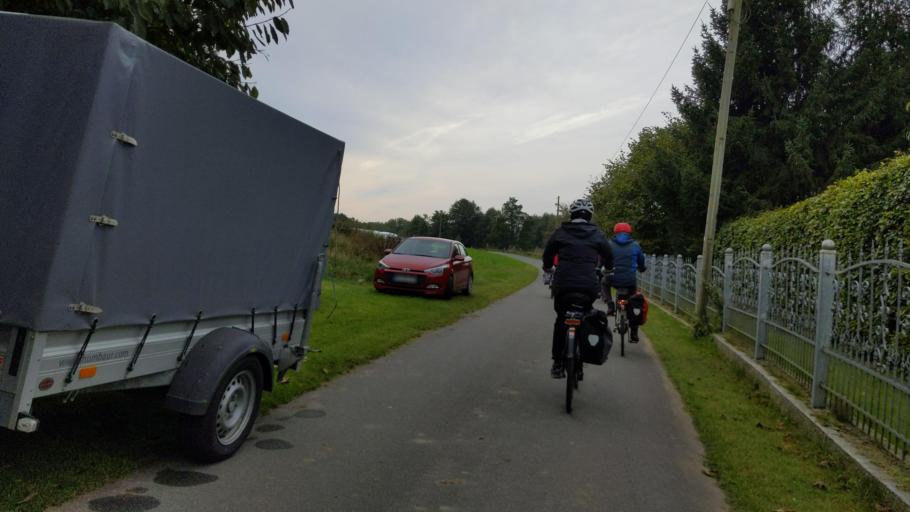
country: DE
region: Schleswig-Holstein
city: Rehhorst
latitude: 53.8638
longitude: 10.4751
